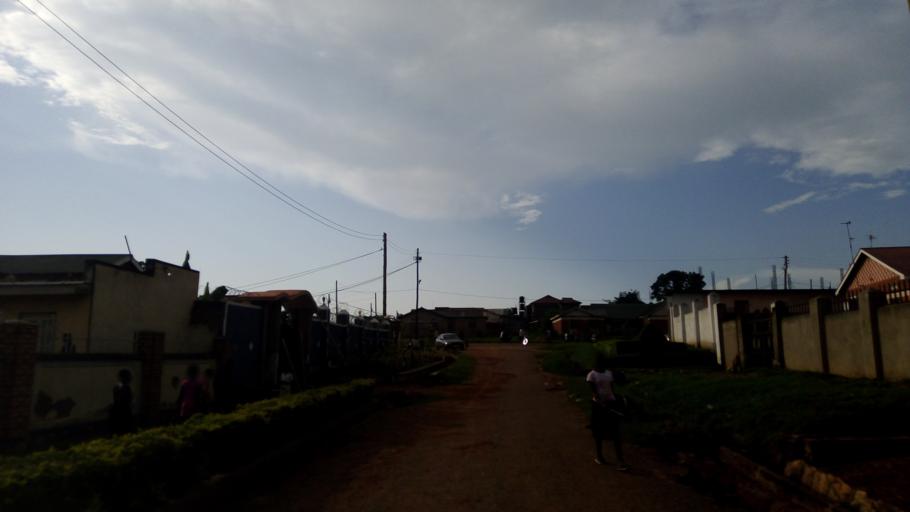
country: UG
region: Eastern Region
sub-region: Mbale District
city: Mbale
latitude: 1.0746
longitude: 34.1675
